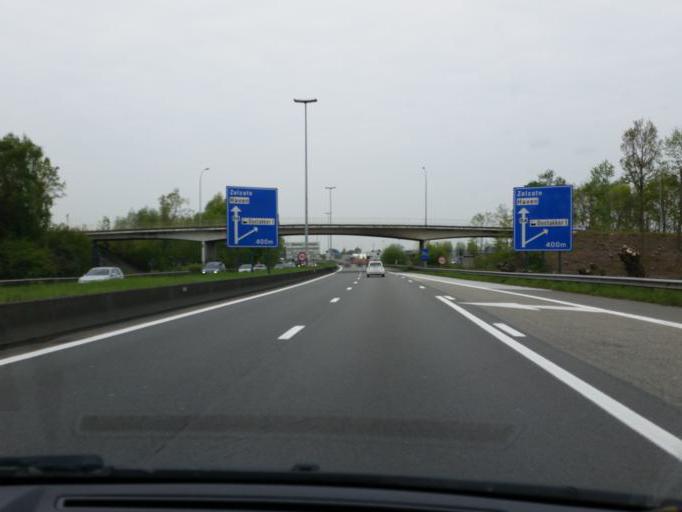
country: BE
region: Flanders
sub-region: Provincie Oost-Vlaanderen
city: Destelbergen
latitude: 51.0853
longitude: 3.7838
